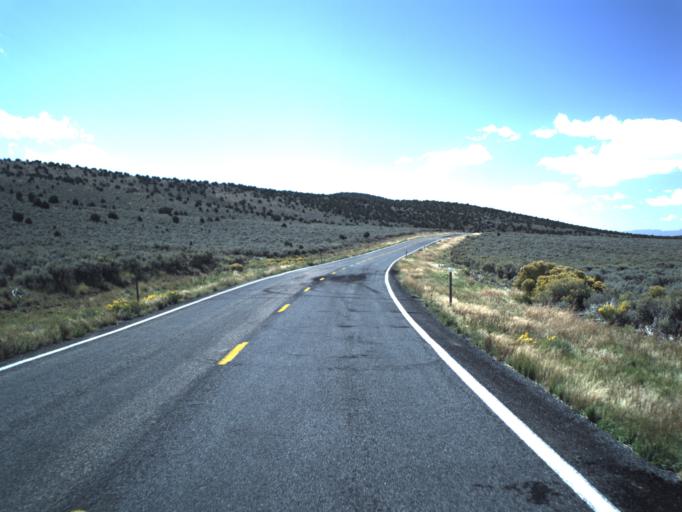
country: US
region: Utah
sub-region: Iron County
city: Parowan
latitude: 38.0579
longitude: -112.9681
